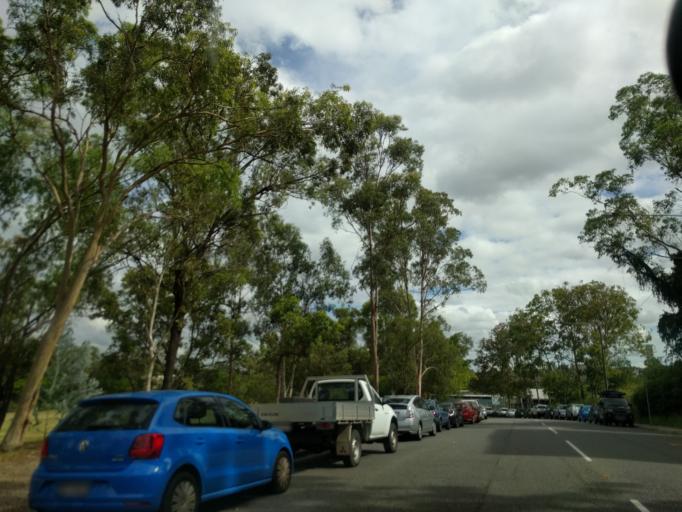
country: AU
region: Queensland
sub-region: Brisbane
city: Yeronga
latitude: -27.4974
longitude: 153.0067
